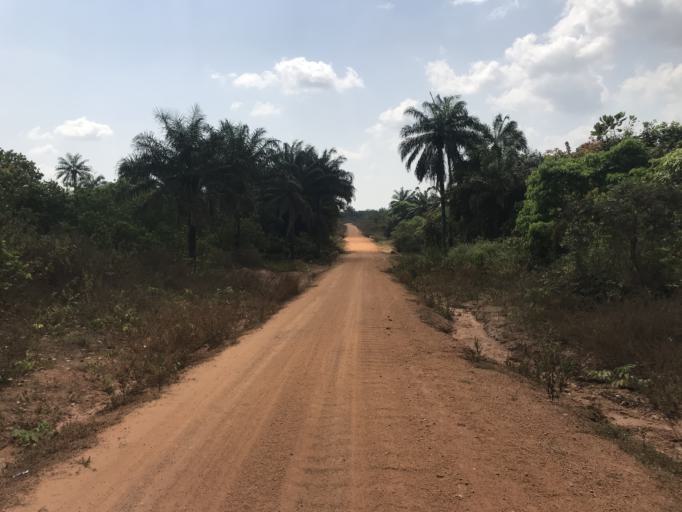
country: NG
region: Osun
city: Ifon
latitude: 7.9779
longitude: 4.5145
